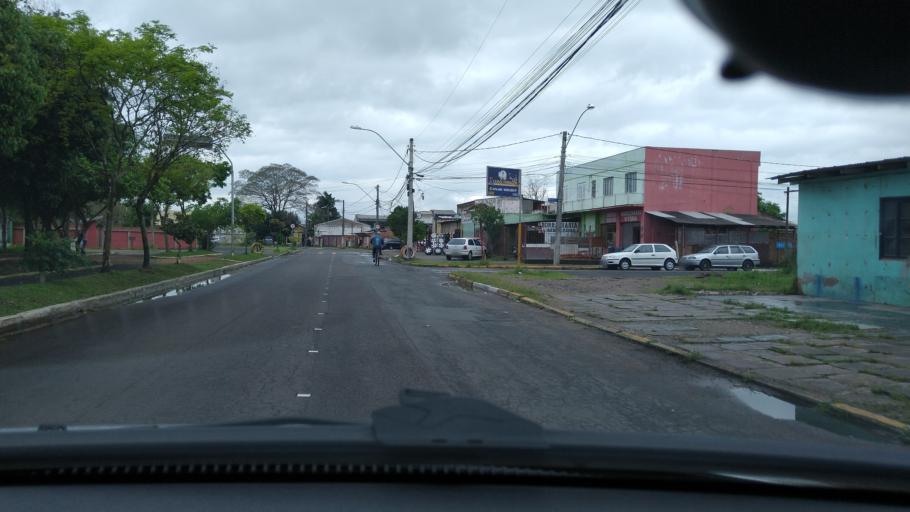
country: BR
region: Rio Grande do Sul
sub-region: Canoas
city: Canoas
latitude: -29.9026
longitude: -51.2048
